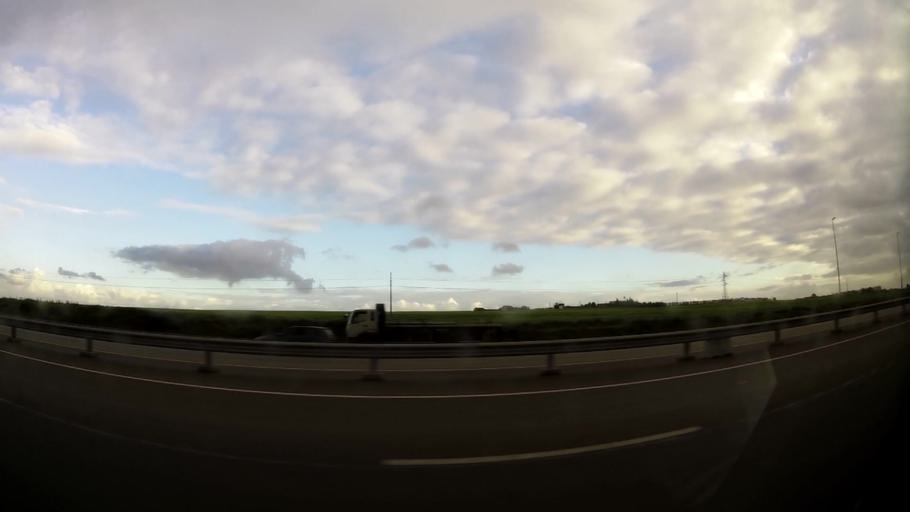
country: MA
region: Grand Casablanca
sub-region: Mediouna
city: Tit Mellil
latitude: 33.5682
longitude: -7.4661
